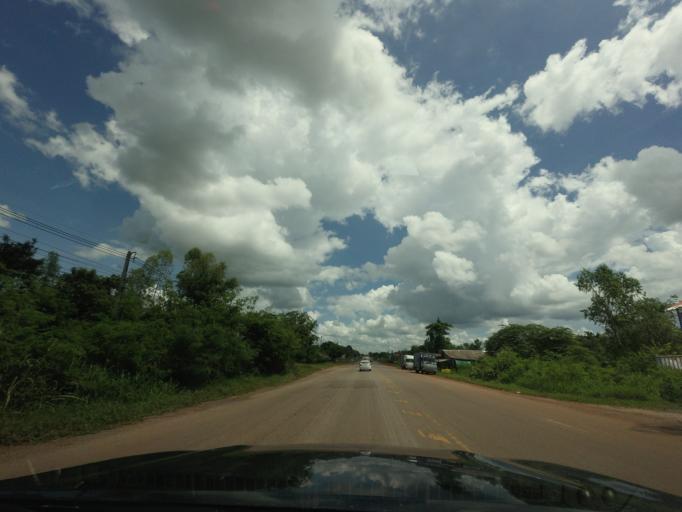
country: TH
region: Changwat Udon Thani
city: Ban Dung
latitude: 17.6783
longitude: 103.2423
